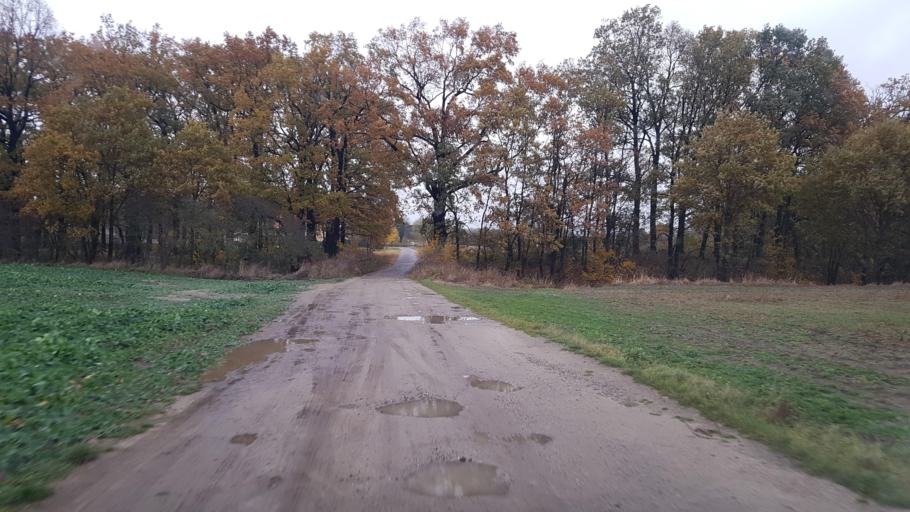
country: DE
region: Brandenburg
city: Drebkau
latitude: 51.6960
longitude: 14.2266
